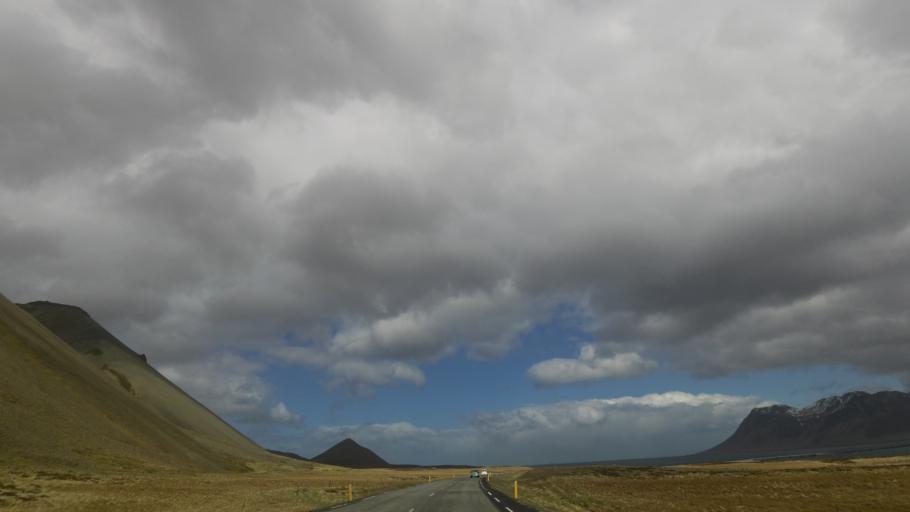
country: IS
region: West
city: Stykkisholmur
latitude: 64.9591
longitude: -23.1519
